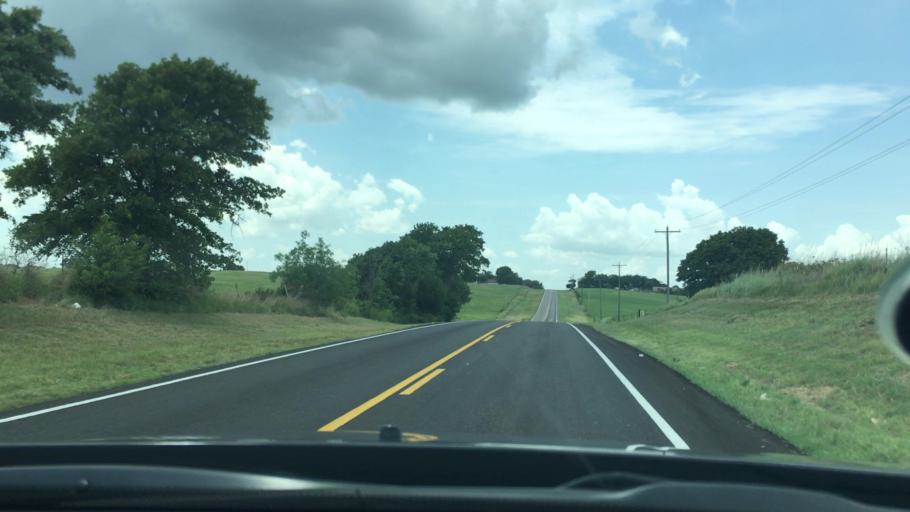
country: US
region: Oklahoma
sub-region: Carter County
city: Wilson
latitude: 33.9403
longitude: -97.3684
